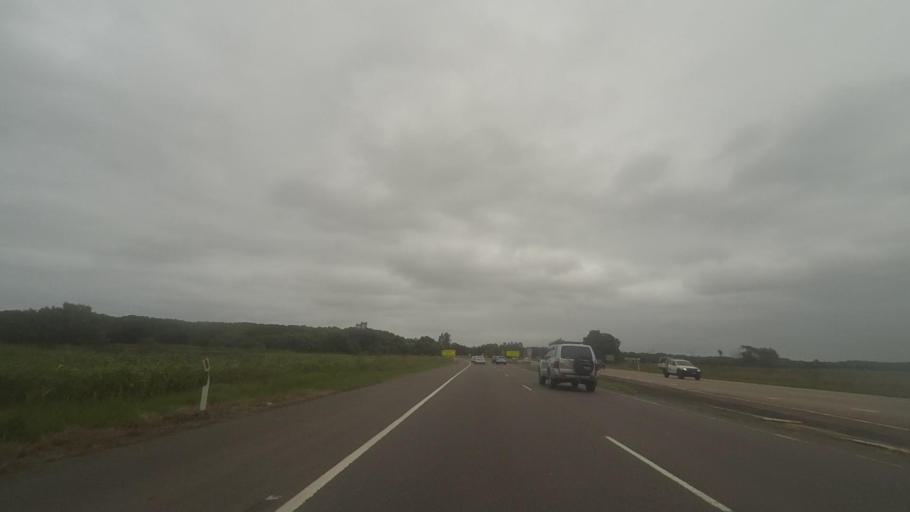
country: AU
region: New South Wales
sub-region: Newcastle
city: Beresfield
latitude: -32.8195
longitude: 151.6901
